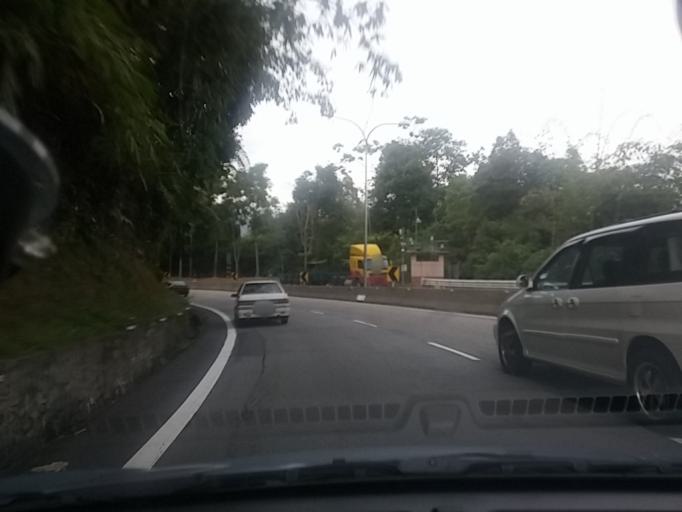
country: MY
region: Pahang
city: Kampung Bukit Tinggi, Bentong
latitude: 3.3755
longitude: 101.7740
